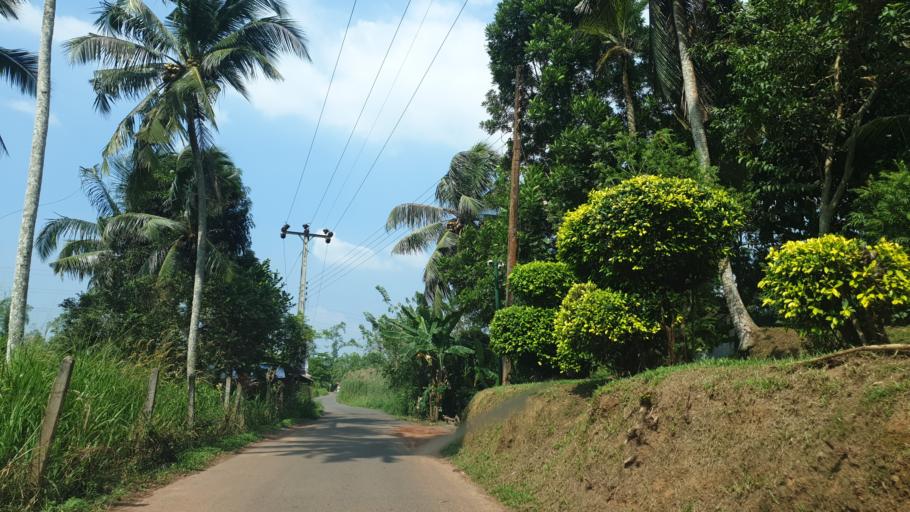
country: LK
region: Western
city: Panadura
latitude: 6.7392
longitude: 79.9515
